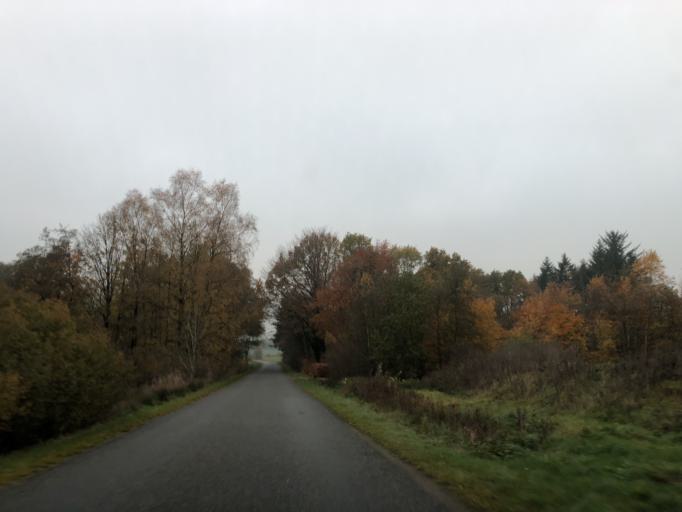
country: DK
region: Central Jutland
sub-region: Herning Kommune
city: Vildbjerg
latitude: 56.2043
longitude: 8.7007
